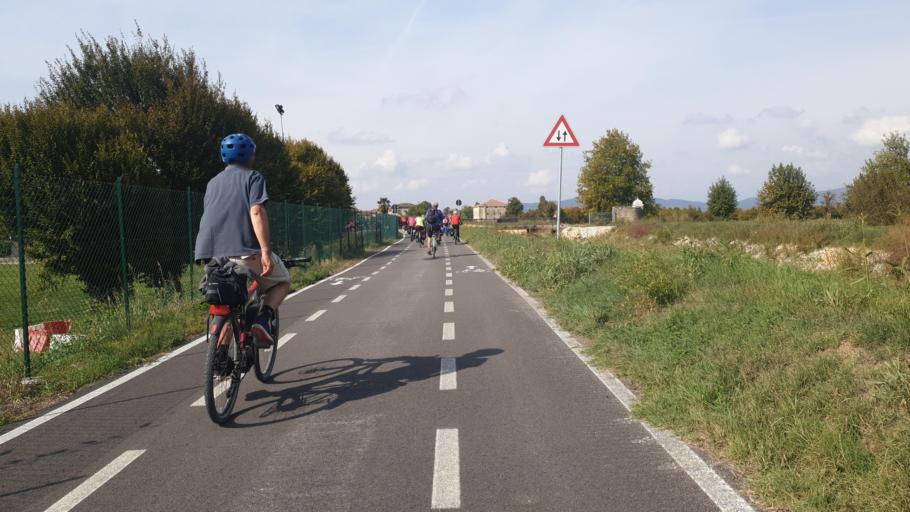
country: IT
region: Veneto
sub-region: Provincia di Vicenza
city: Agugliaro
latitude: 45.3261
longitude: 11.5861
